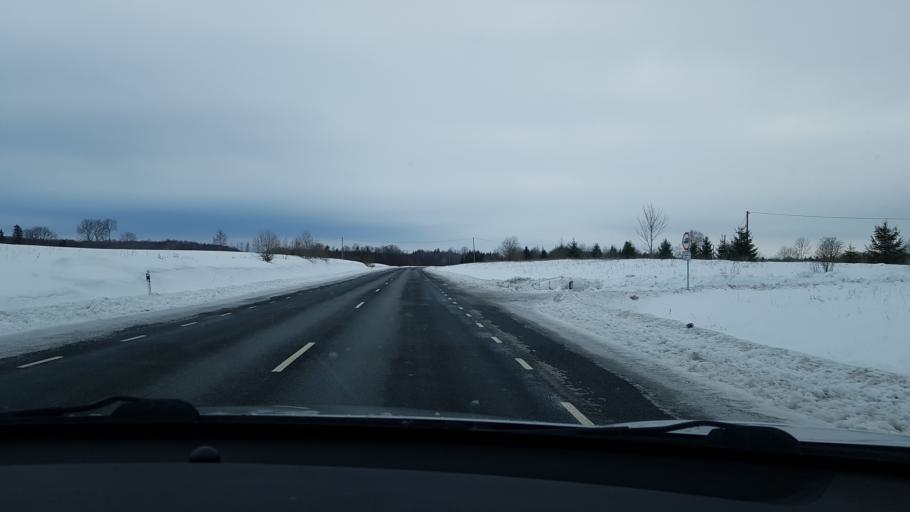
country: EE
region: Jaervamaa
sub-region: Jaerva-Jaani vald
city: Jarva-Jaani
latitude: 58.8998
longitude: 25.7996
